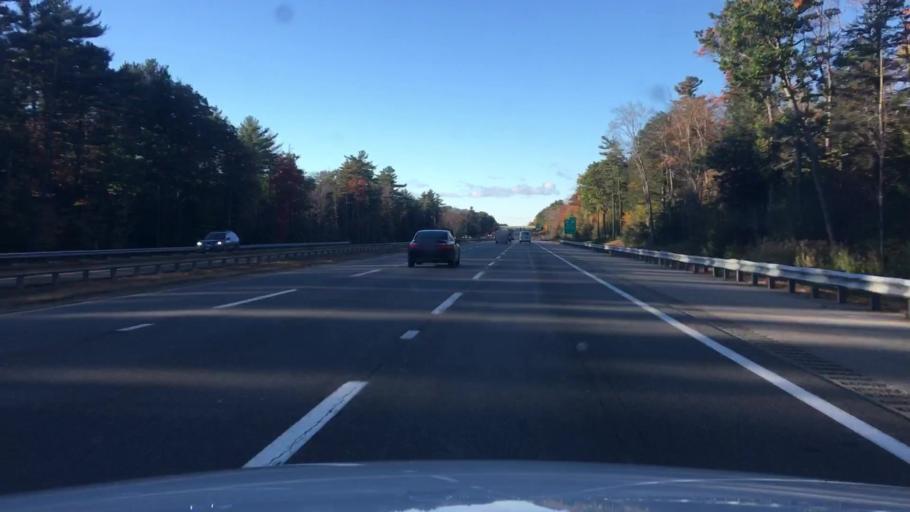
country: US
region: Maine
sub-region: York County
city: Wells Beach Station
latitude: 43.3450
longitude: -70.5962
